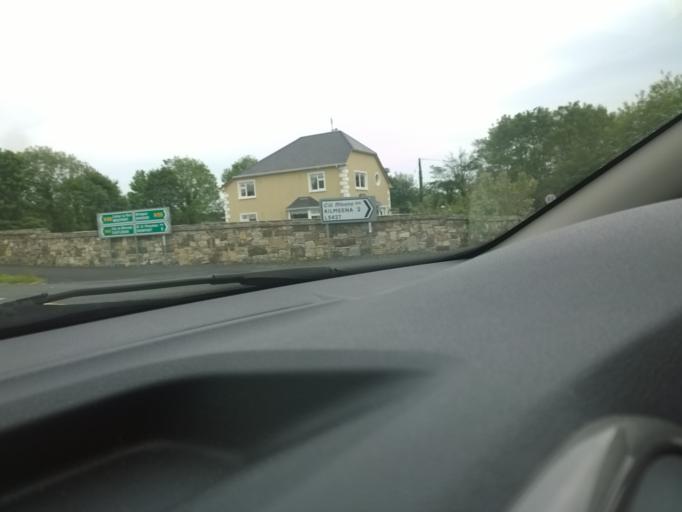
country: IE
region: Connaught
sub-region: Maigh Eo
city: Westport
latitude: 53.8464
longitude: -9.5502
